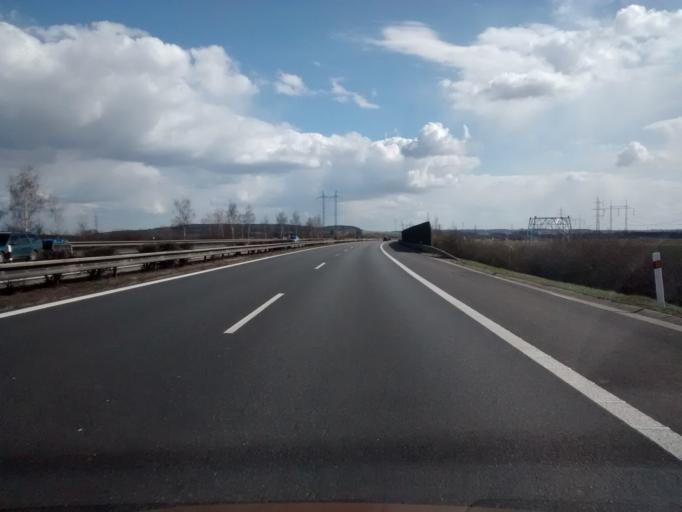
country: CZ
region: Central Bohemia
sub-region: Okres Melnik
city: Veltrusy
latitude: 50.2961
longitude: 14.3440
